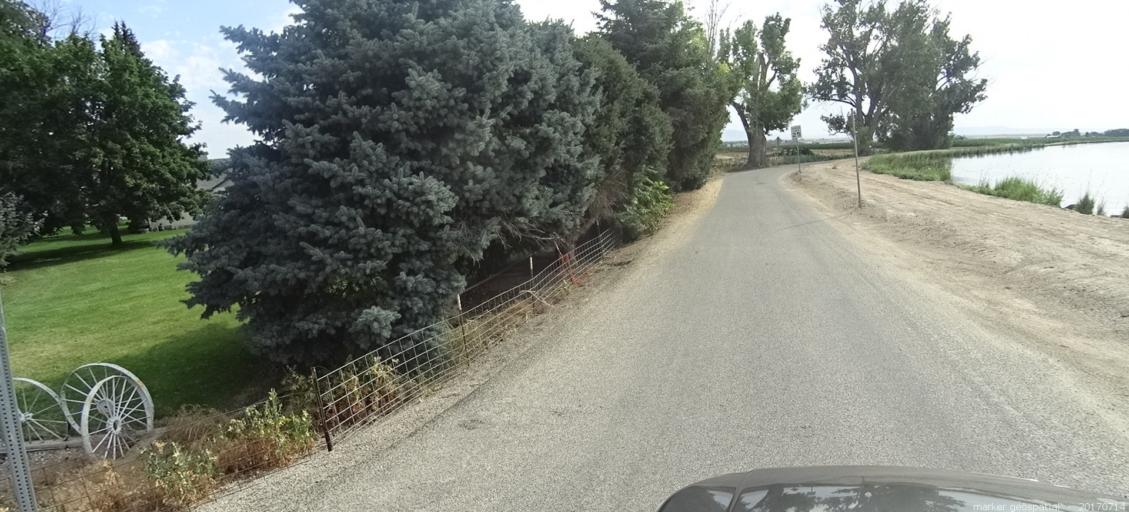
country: US
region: Idaho
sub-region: Ada County
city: Kuna
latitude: 43.4620
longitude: -116.3744
